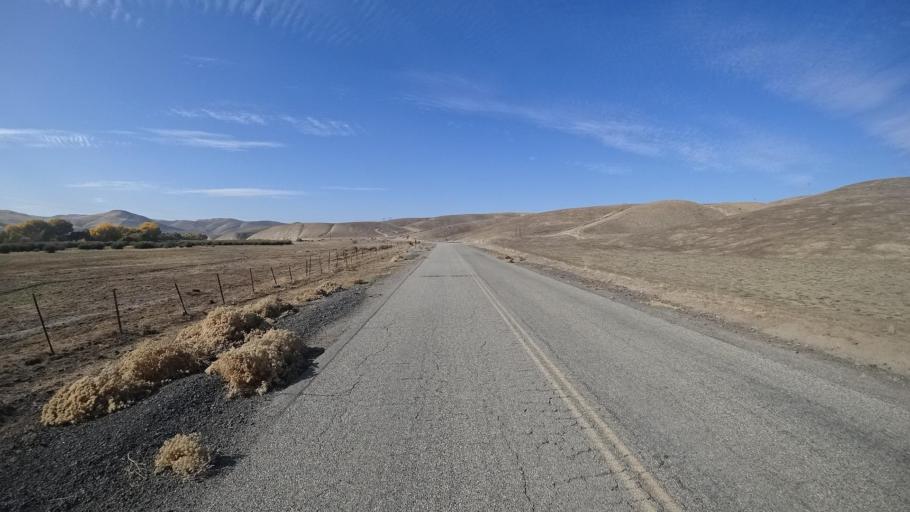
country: US
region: California
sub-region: Kern County
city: Oildale
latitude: 35.5172
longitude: -118.9139
